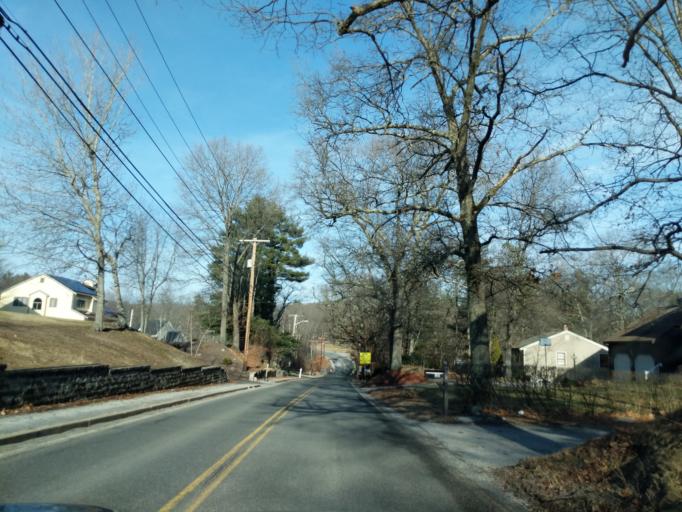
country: US
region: Massachusetts
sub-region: Worcester County
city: Blackstone
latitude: 42.0301
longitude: -71.5421
